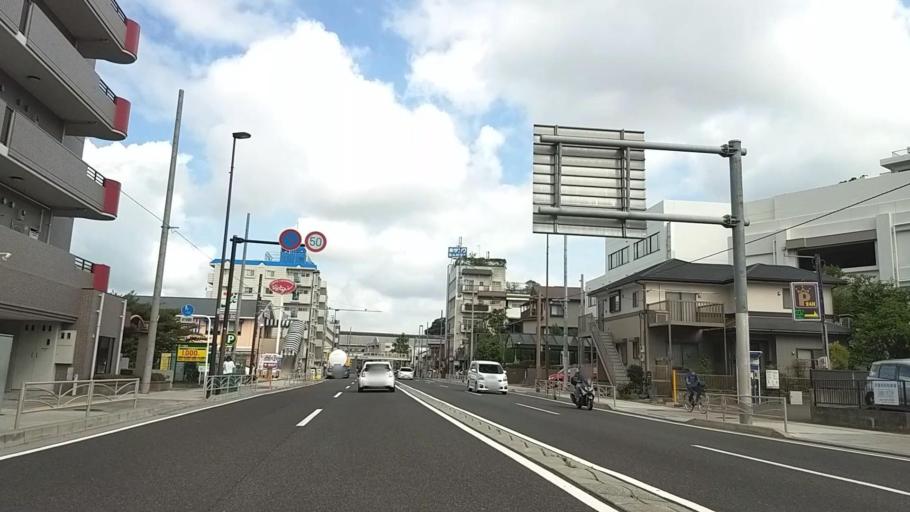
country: JP
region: Kanagawa
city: Yokohama
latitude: 35.4665
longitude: 139.5823
